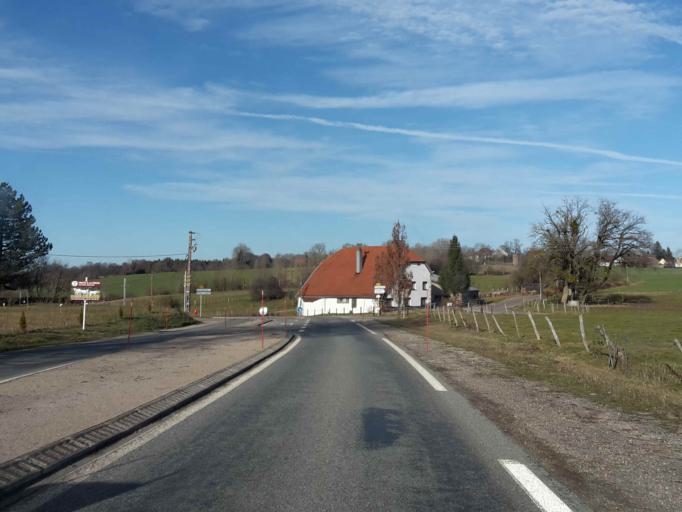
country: FR
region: Franche-Comte
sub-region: Departement du Doubs
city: Vercel-Villedieu-le-Camp
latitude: 47.2108
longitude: 6.3928
